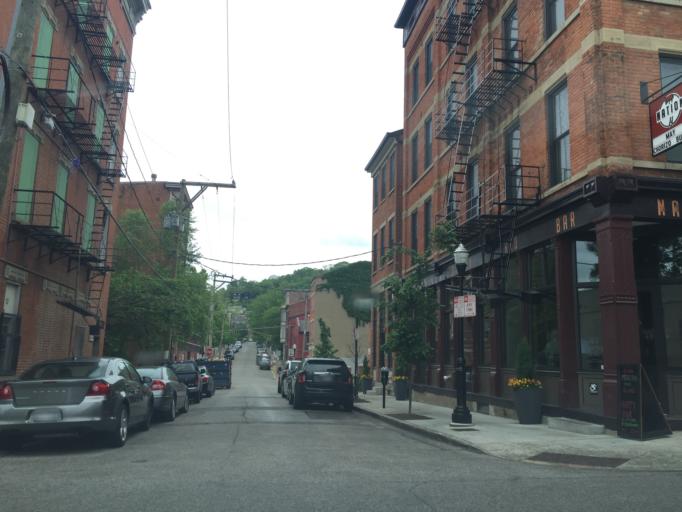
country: US
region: Kentucky
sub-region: Campbell County
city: Newport
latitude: 39.1096
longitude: -84.5084
